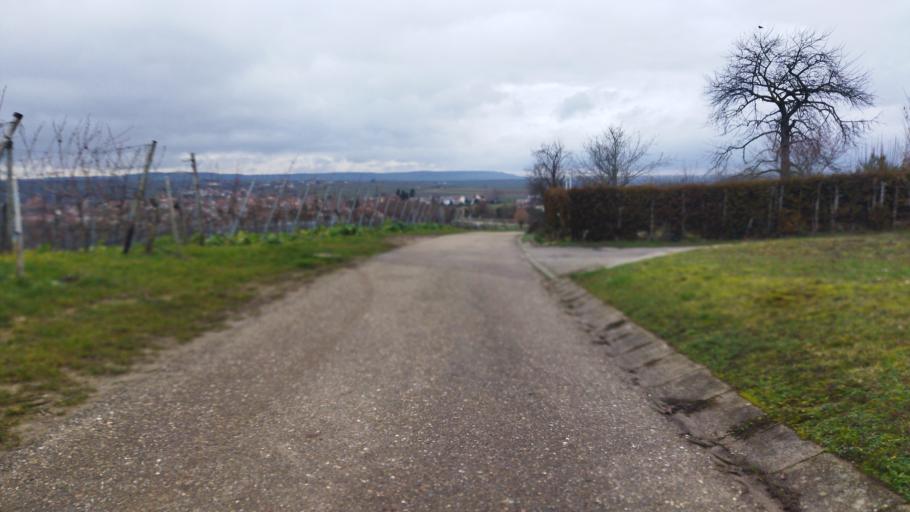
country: DE
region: Baden-Wuerttemberg
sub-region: Regierungsbezirk Stuttgart
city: Talheim
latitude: 49.0722
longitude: 9.1752
